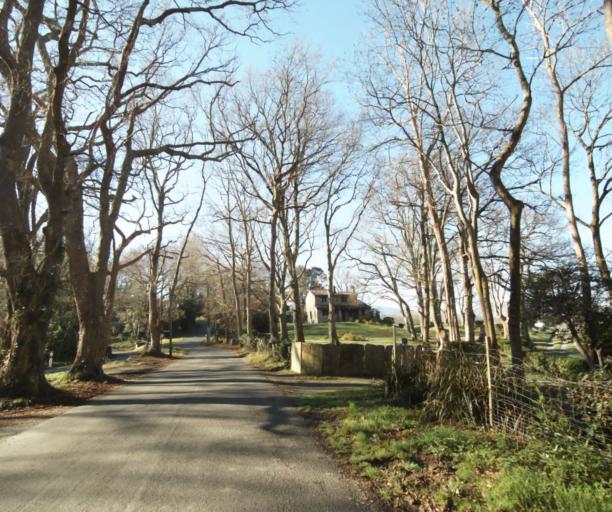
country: FR
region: Aquitaine
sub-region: Departement des Pyrenees-Atlantiques
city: Ciboure
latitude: 43.3638
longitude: -1.6608
